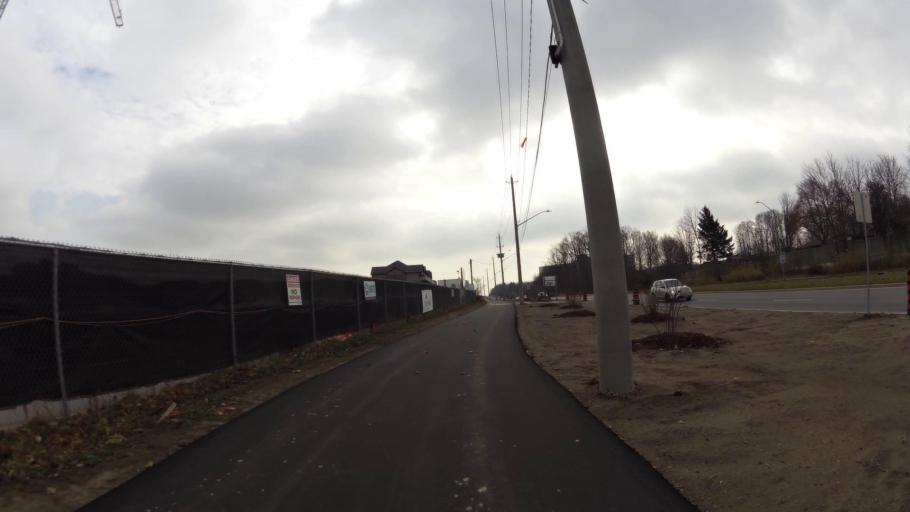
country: CA
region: Ontario
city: Kitchener
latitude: 43.4174
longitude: -80.4703
